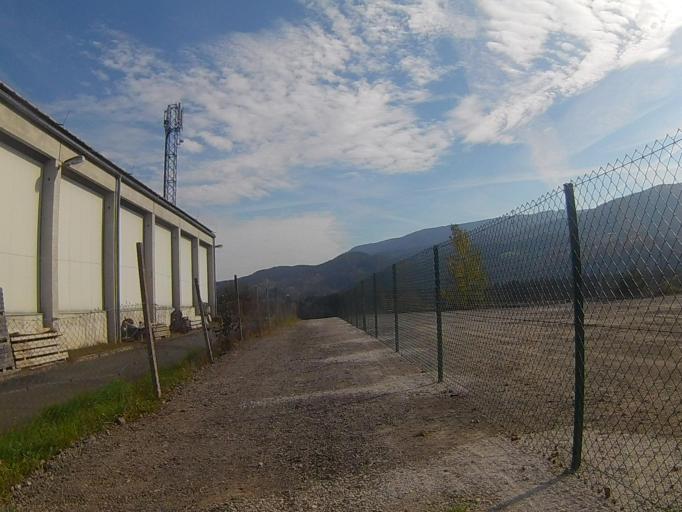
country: SI
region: Selnica ob Dravi
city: Selnica ob Dravi
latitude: 46.5443
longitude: 15.4890
